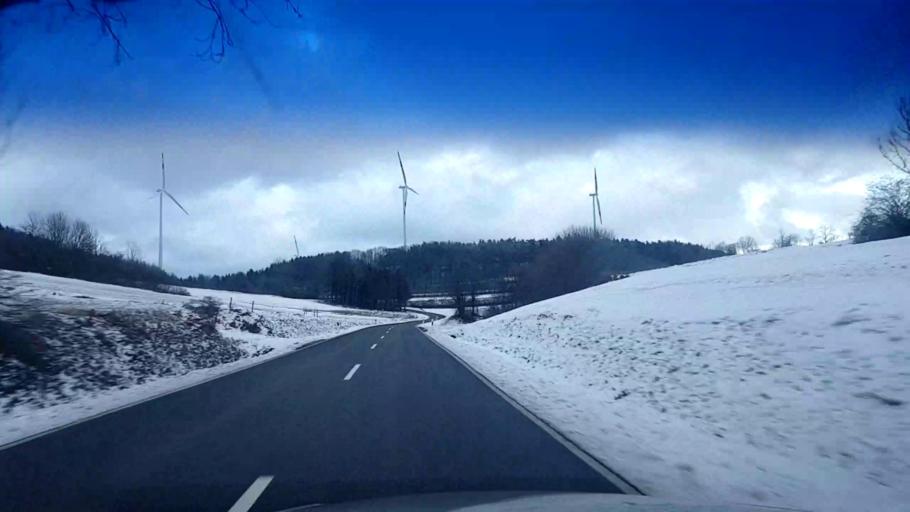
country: DE
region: Bavaria
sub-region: Upper Franconia
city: Buttenheim
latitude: 49.8528
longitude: 11.0824
